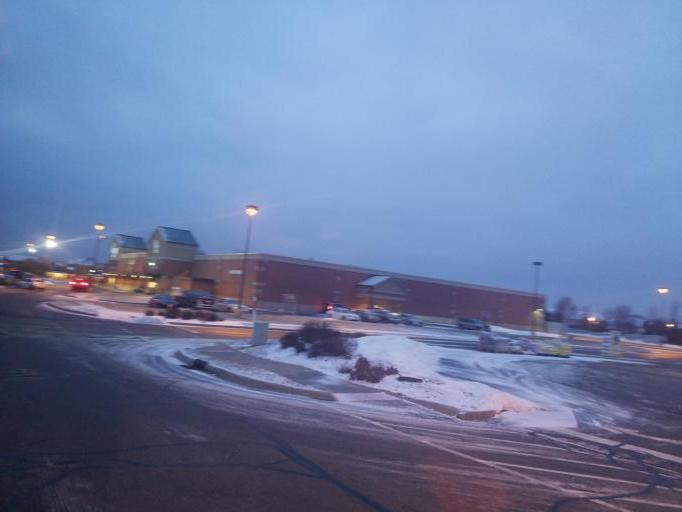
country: US
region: Ohio
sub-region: Delaware County
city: Sunbury
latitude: 40.2467
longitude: -82.8674
